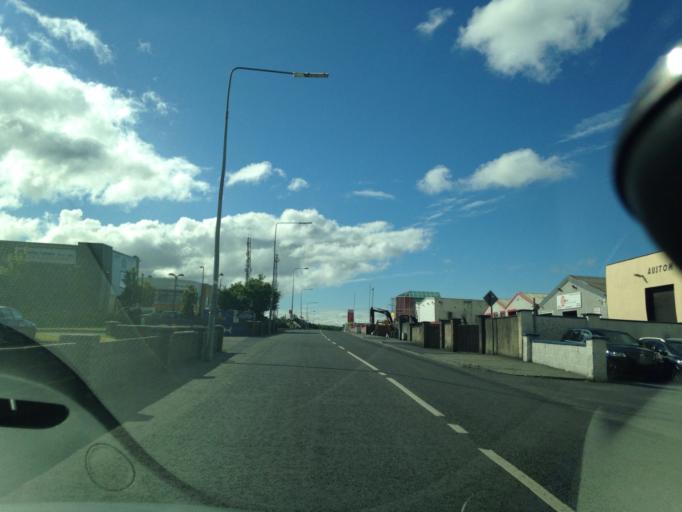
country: IE
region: Connaught
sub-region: County Galway
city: Gaillimh
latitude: 53.2925
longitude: -9.0171
